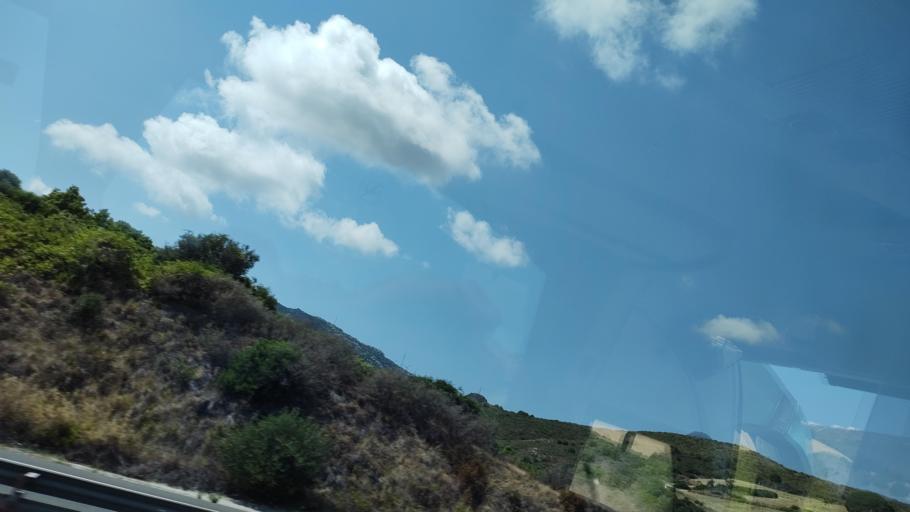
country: ES
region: Andalusia
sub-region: Provincia de Malaga
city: Manilva
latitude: 36.3935
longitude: -5.2522
